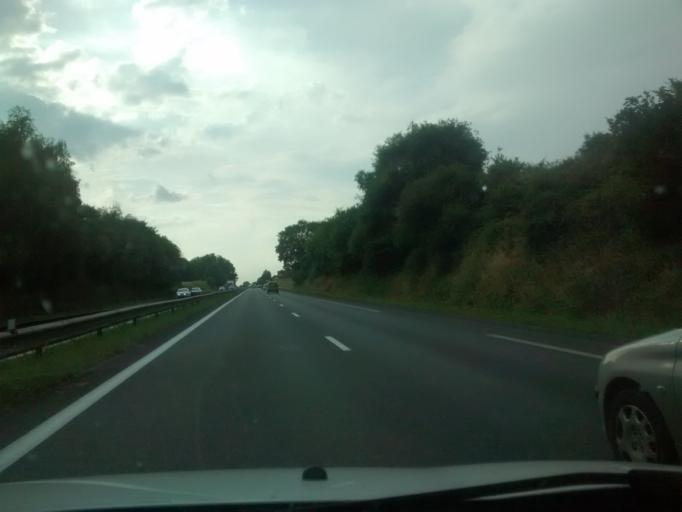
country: FR
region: Brittany
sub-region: Departement des Cotes-d'Armor
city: Graces
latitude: 48.5582
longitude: -3.1808
